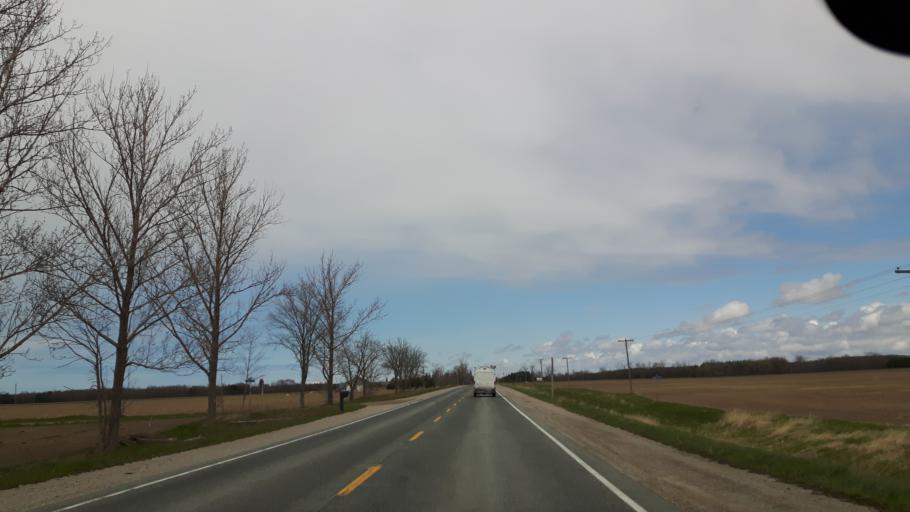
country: CA
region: Ontario
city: Bluewater
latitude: 43.5042
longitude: -81.6951
